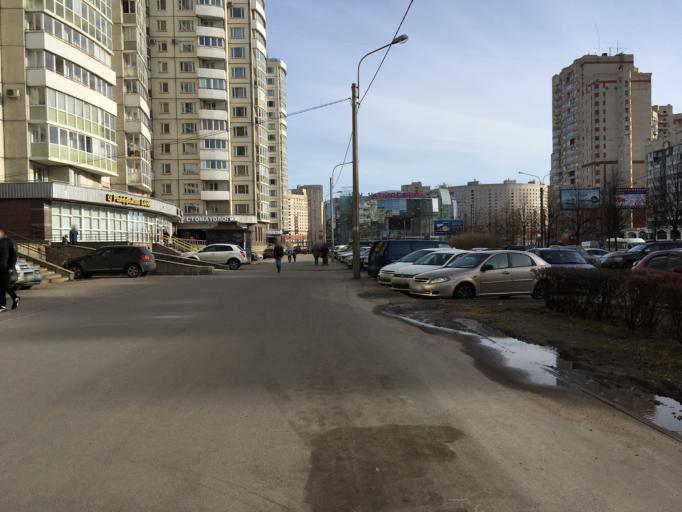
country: RU
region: St.-Petersburg
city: Komendantsky aerodrom
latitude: 60.0106
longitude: 30.2573
